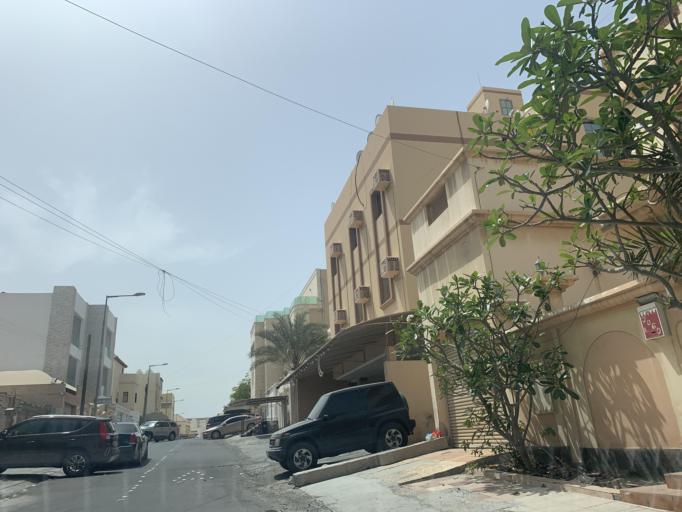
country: BH
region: Northern
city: Ar Rifa'
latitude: 26.1310
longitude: 50.5794
